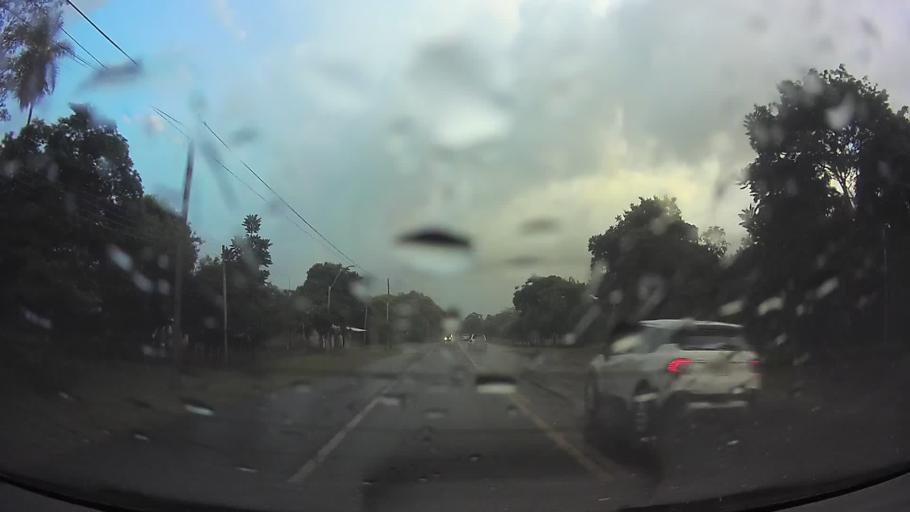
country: PY
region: Paraguari
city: Yaguaron
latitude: -25.5807
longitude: -57.2529
